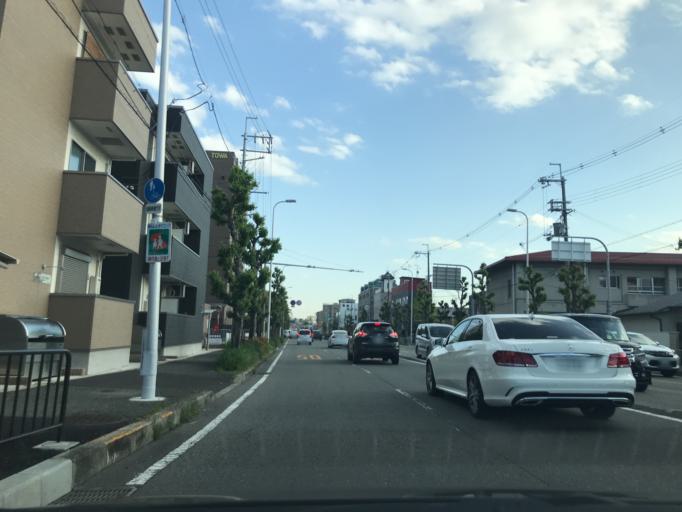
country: JP
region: Osaka
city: Ikeda
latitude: 34.8107
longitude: 135.4401
